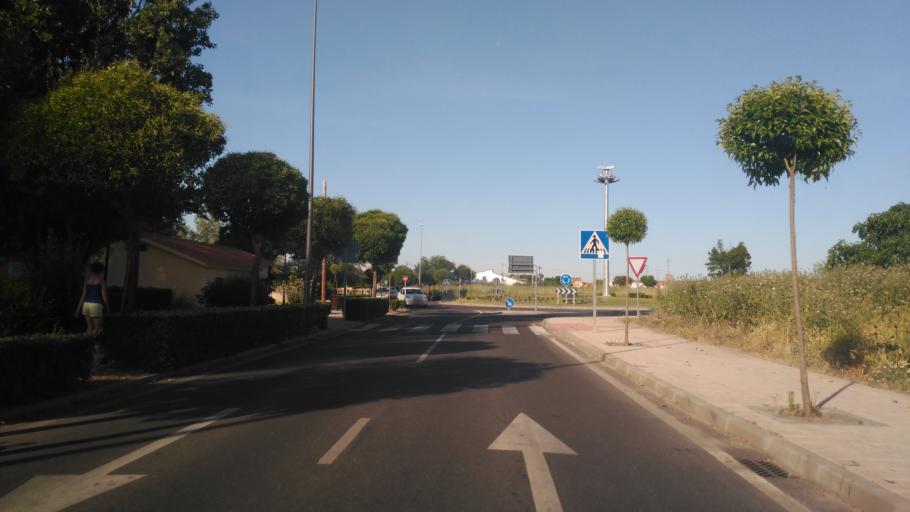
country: ES
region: Castille and Leon
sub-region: Provincia de Zamora
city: Zamora
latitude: 41.4950
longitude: -5.7540
